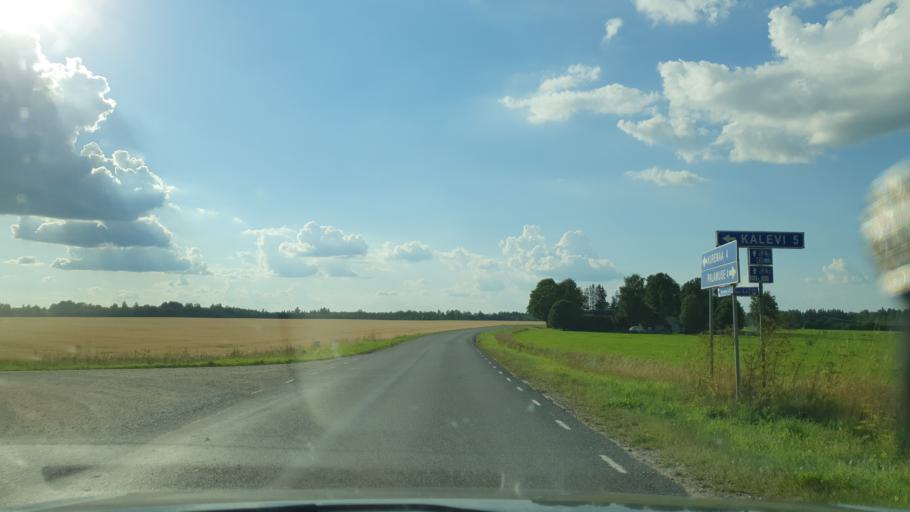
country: EE
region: Jogevamaa
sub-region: Jogeva linn
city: Jogeva
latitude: 58.7079
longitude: 26.5373
